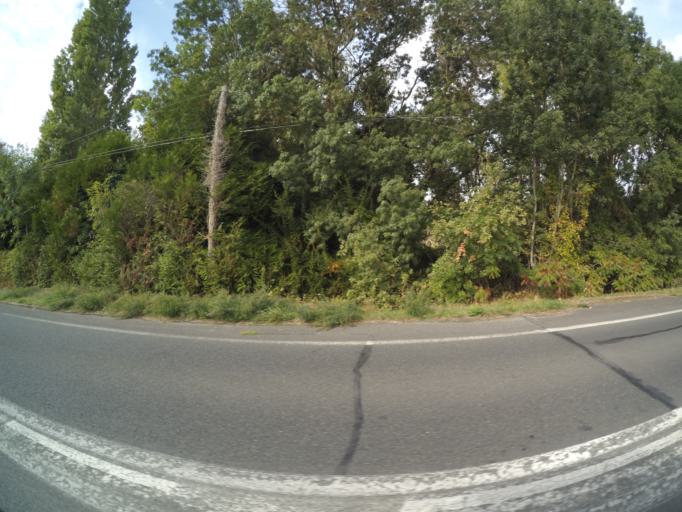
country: FR
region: Centre
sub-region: Departement d'Indre-et-Loire
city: Langeais
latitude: 47.3016
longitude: 0.3508
